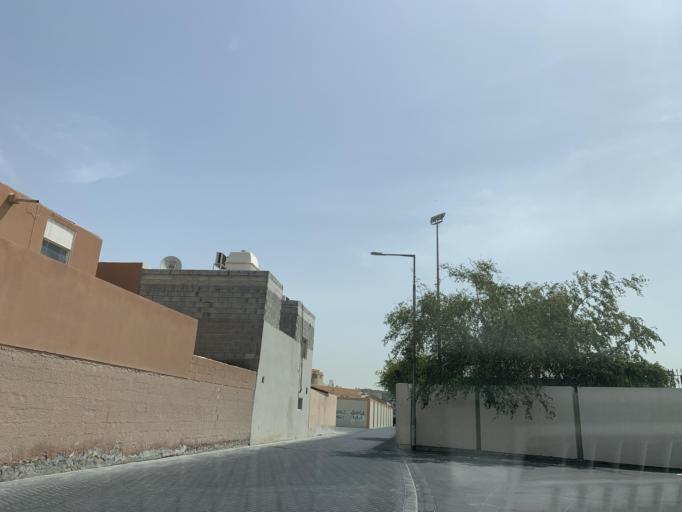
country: BH
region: Northern
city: Madinat `Isa
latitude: 26.1709
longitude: 50.5613
